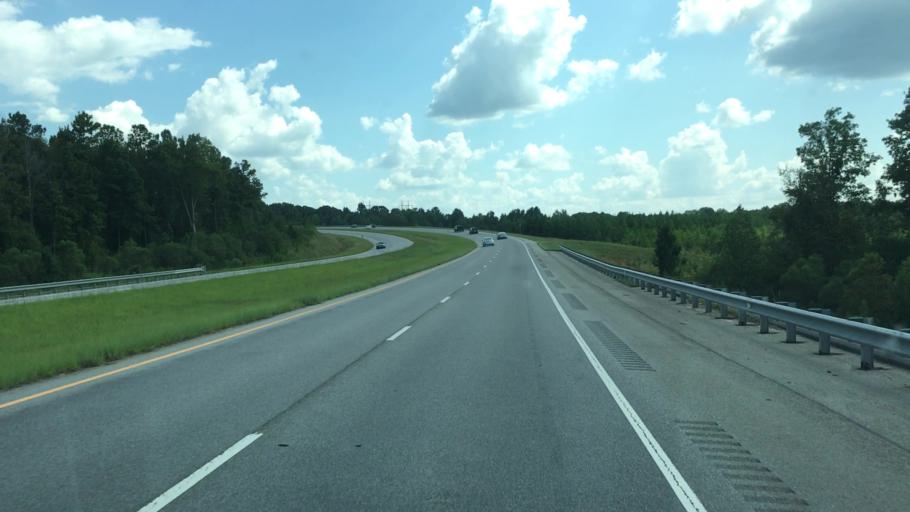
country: US
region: Georgia
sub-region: Putnam County
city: Eatonton
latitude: 33.2799
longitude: -83.3708
